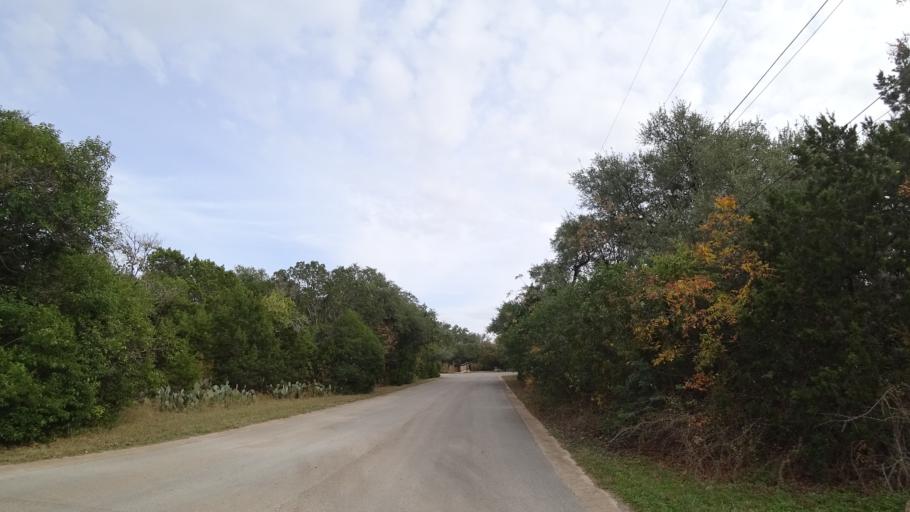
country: US
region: Texas
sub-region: Williamson County
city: Round Rock
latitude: 30.5141
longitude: -97.6595
